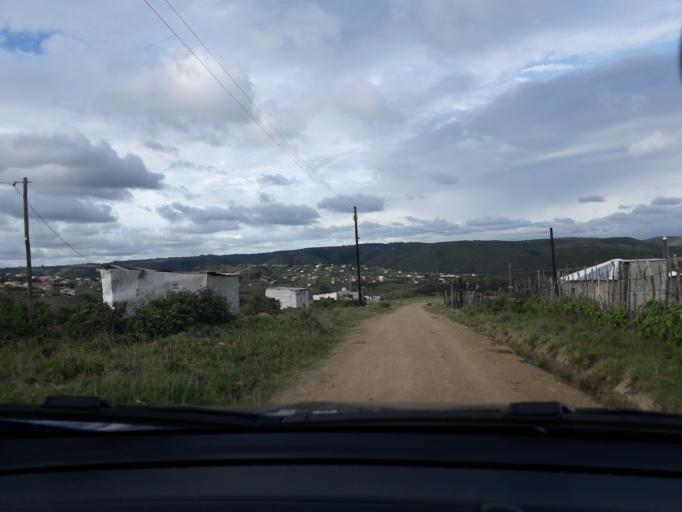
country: ZA
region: Eastern Cape
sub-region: Buffalo City Metropolitan Municipality
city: East London
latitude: -32.8037
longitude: 27.9663
